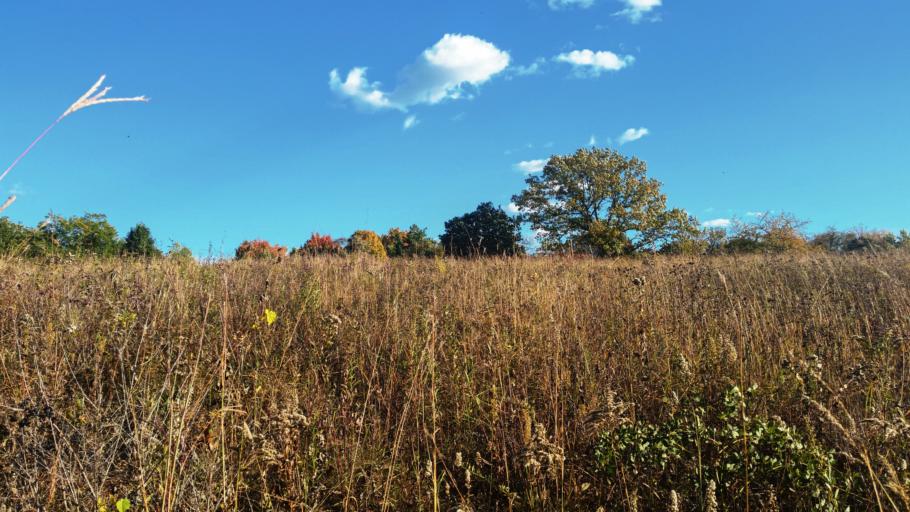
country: US
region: Wisconsin
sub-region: Dane County
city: Shorewood Hills
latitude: 43.0443
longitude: -89.4316
